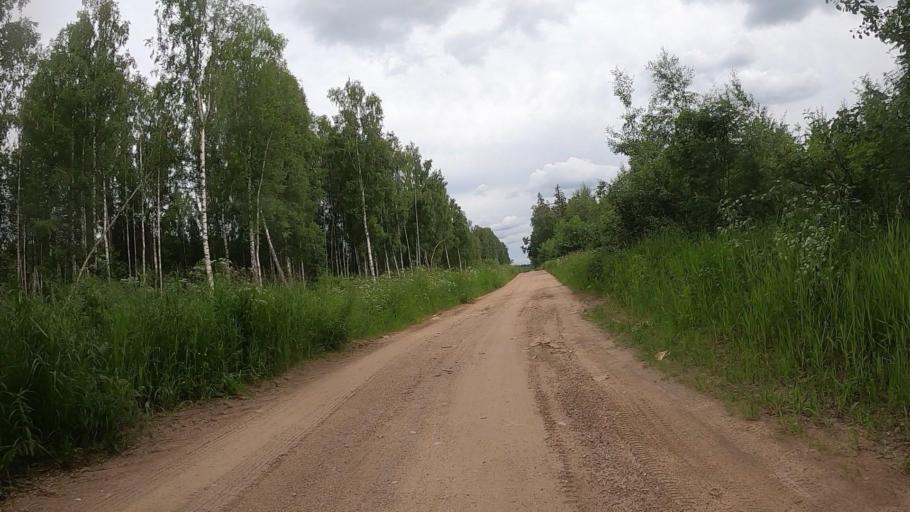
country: LV
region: Olaine
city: Olaine
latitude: 56.8290
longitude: 23.9370
